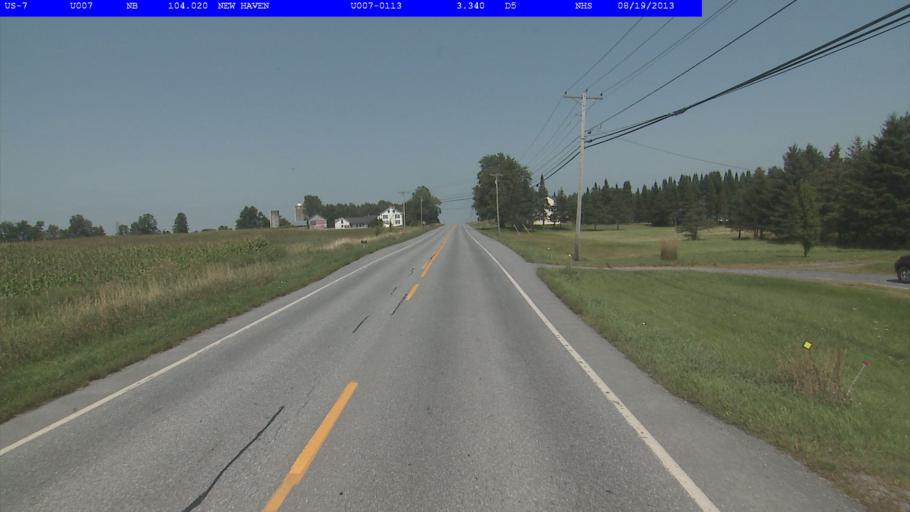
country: US
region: Vermont
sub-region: Addison County
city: Middlebury (village)
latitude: 44.0935
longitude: -73.1739
